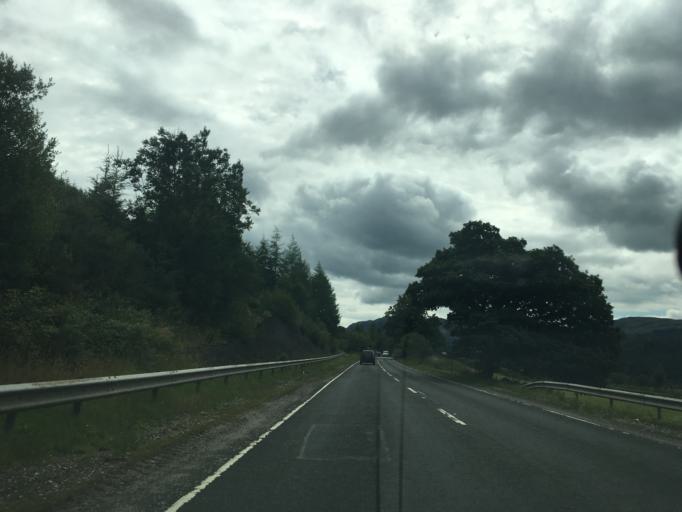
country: GB
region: Scotland
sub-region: Stirling
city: Callander
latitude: 56.3457
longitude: -4.3273
